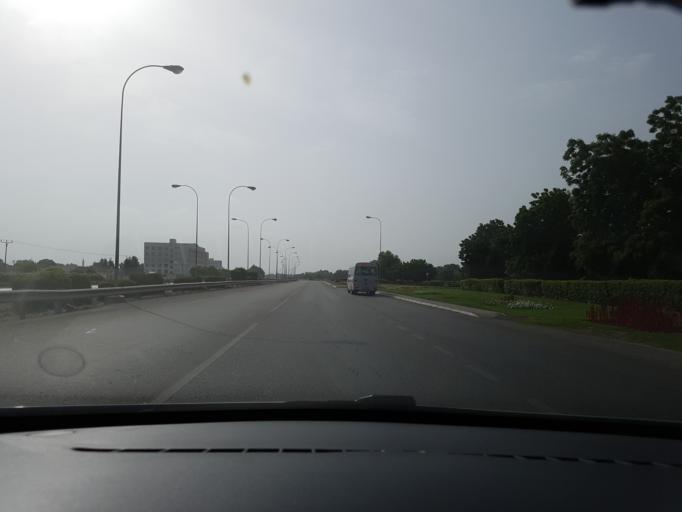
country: OM
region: Al Batinah
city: Al Sohar
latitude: 24.4000
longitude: 56.6647
